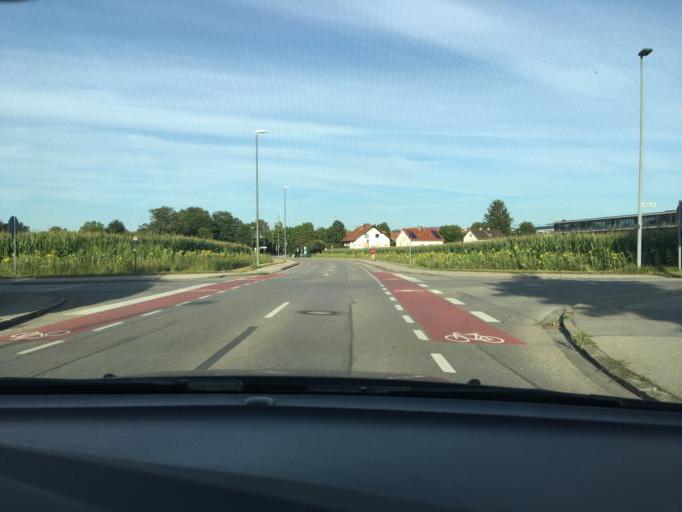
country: DE
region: Bavaria
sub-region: Upper Bavaria
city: Erding
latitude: 48.3121
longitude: 11.8963
